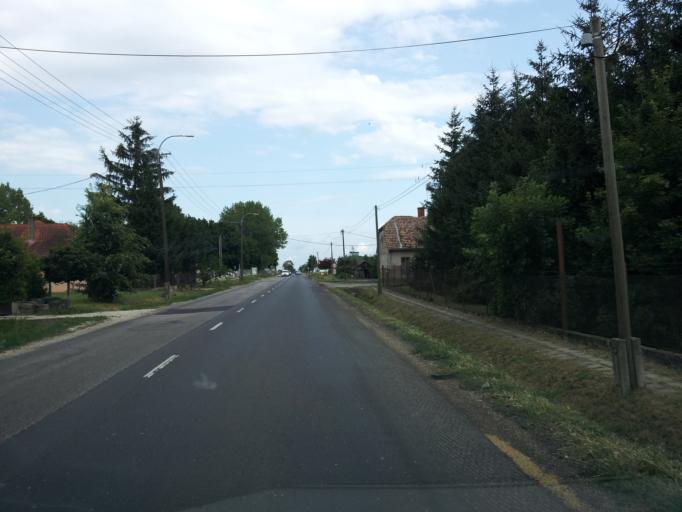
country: HU
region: Fejer
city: Enying
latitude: 46.9206
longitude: 18.2626
